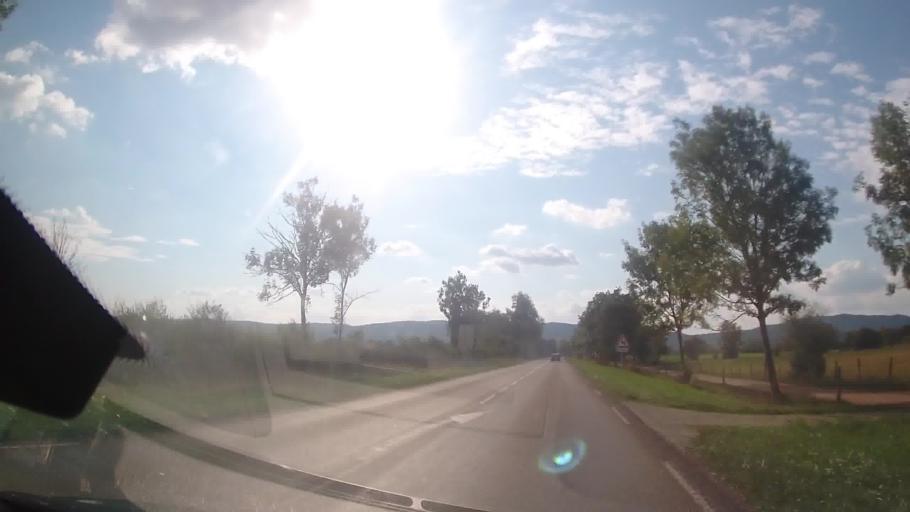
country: FR
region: Franche-Comte
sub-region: Departement du Jura
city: Clairvaux-les-Lacs
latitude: 46.5895
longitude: 5.7122
